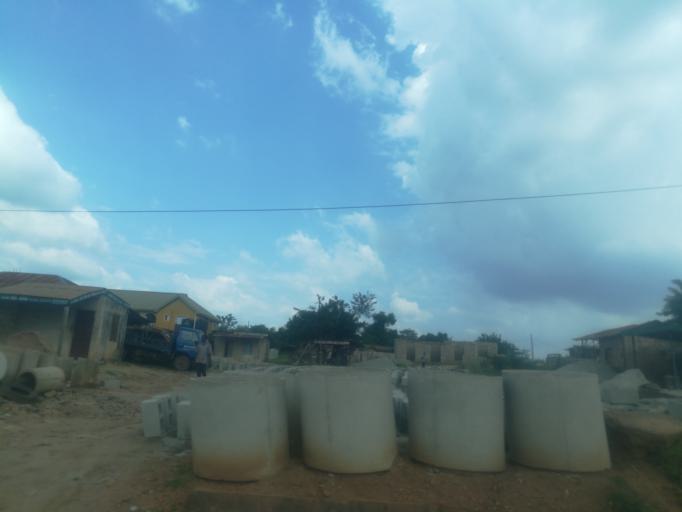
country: NG
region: Oyo
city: Ido
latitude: 7.4315
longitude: 3.8357
